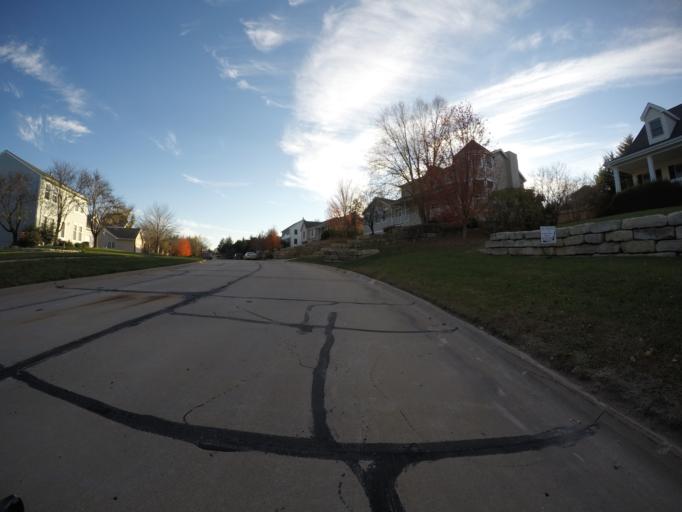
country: US
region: Kansas
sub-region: Riley County
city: Manhattan
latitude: 39.2005
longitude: -96.6349
